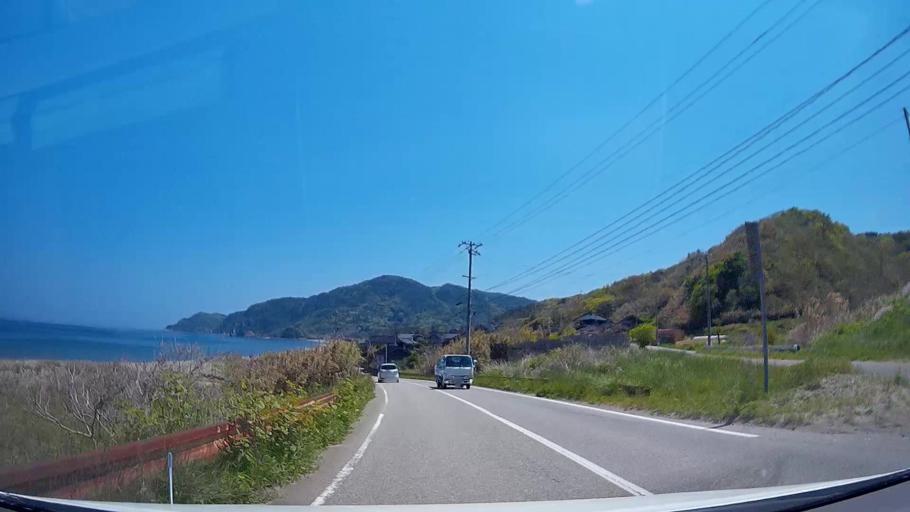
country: JP
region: Ishikawa
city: Nanao
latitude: 37.4482
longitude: 137.0543
